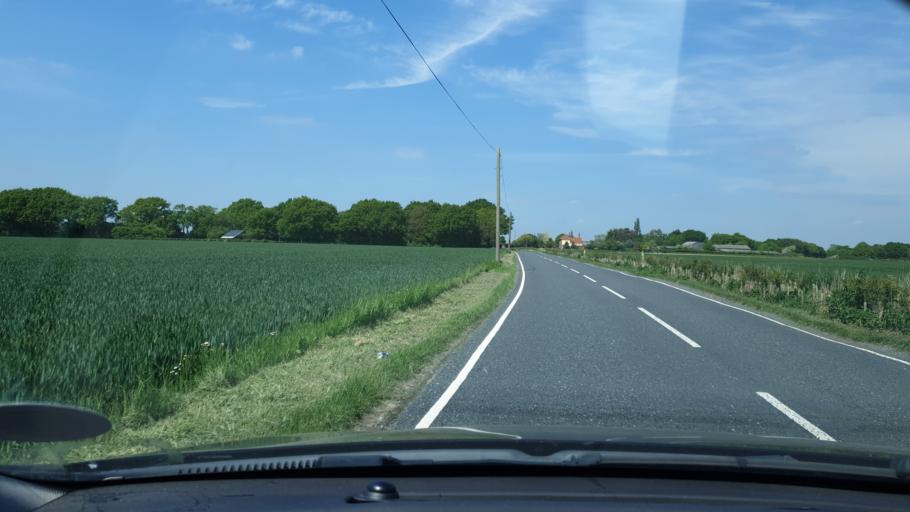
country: GB
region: England
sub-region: Essex
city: Manningtree
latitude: 51.9067
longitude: 1.0583
